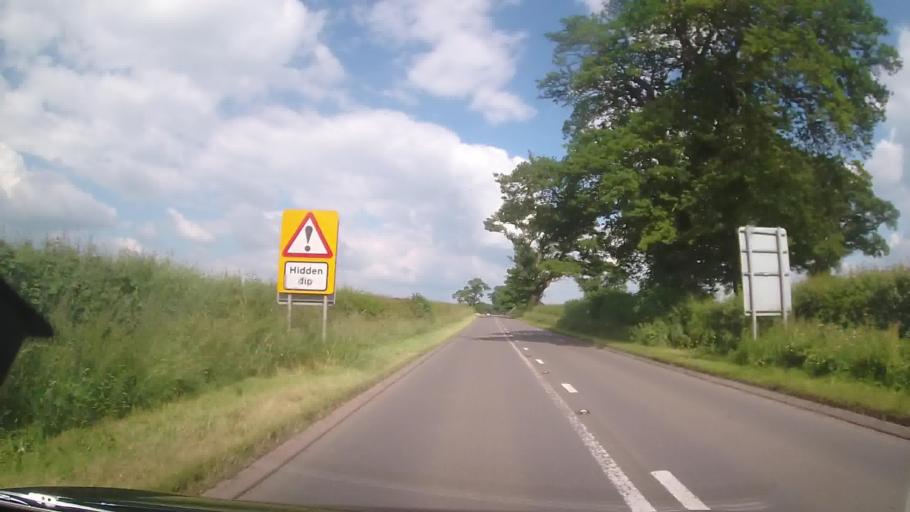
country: GB
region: England
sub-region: Shropshire
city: Whittington
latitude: 52.8844
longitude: -2.9787
